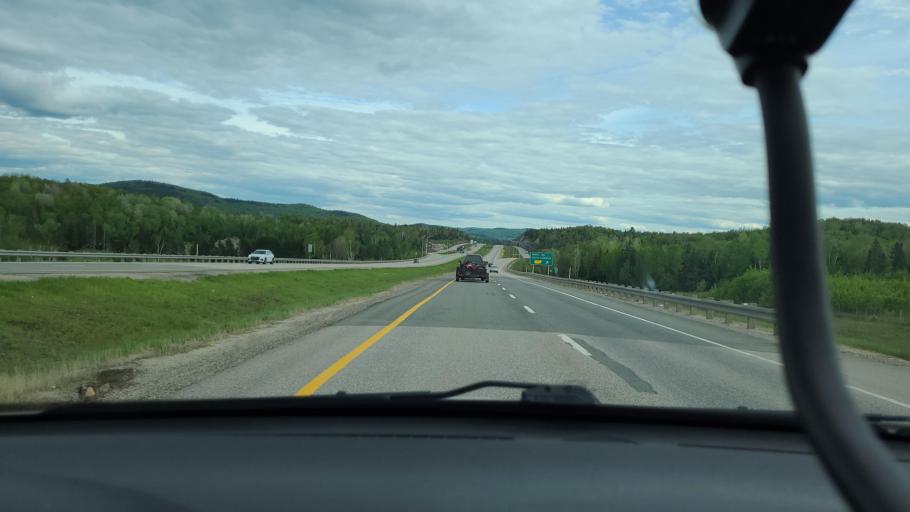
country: CA
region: Quebec
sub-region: Laurentides
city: Labelle
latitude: 46.2636
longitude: -74.7298
